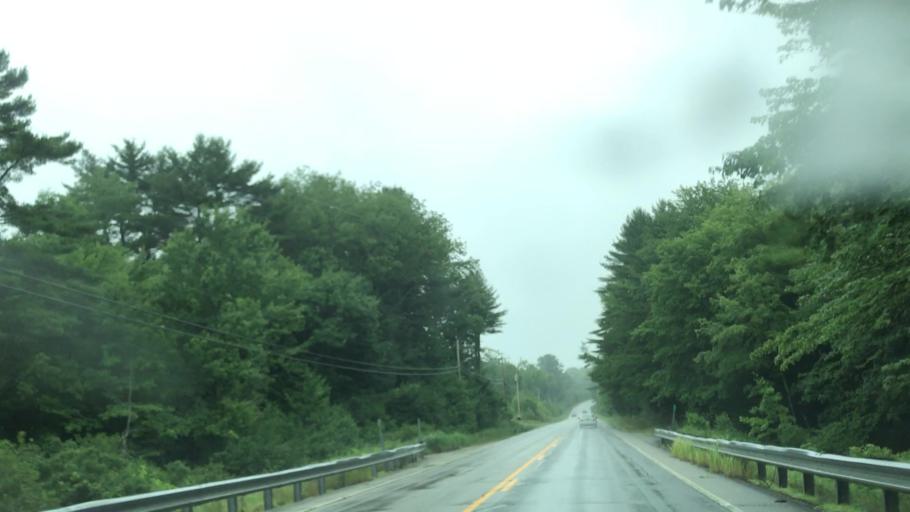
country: US
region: Maine
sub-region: York County
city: North Berwick
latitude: 43.2992
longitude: -70.7722
